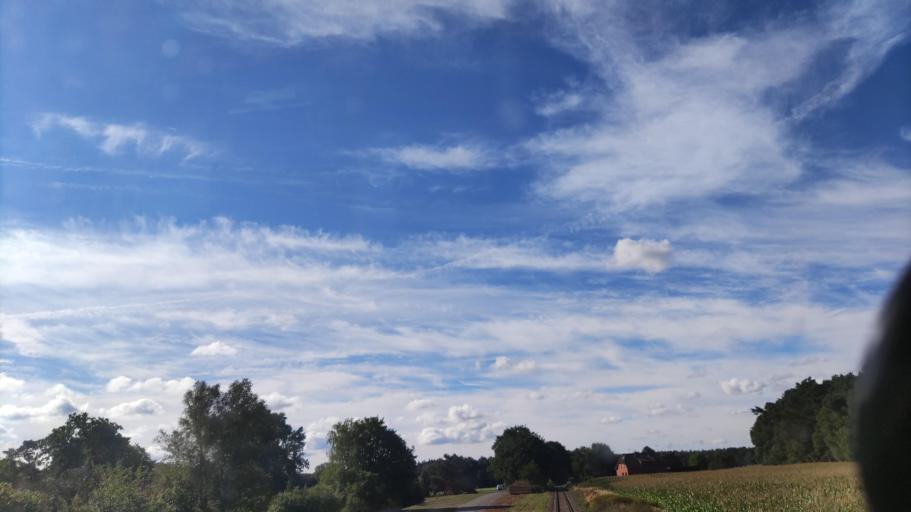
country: DE
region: Lower Saxony
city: Soltau
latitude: 52.9899
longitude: 9.8857
